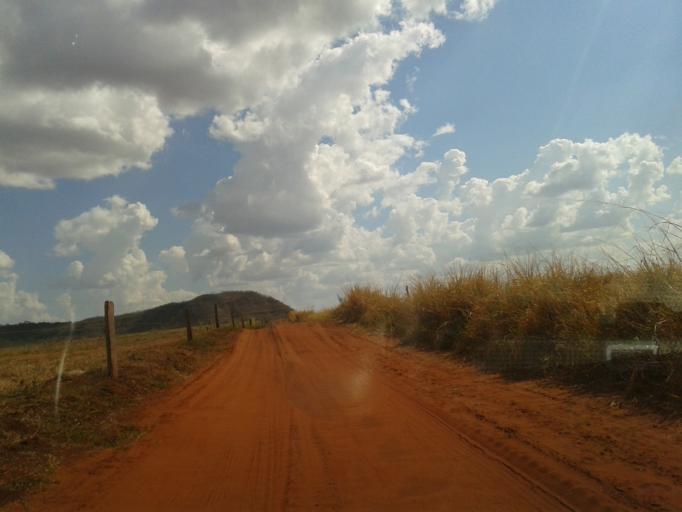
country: BR
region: Minas Gerais
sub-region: Santa Vitoria
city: Santa Vitoria
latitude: -19.1972
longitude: -49.9259
